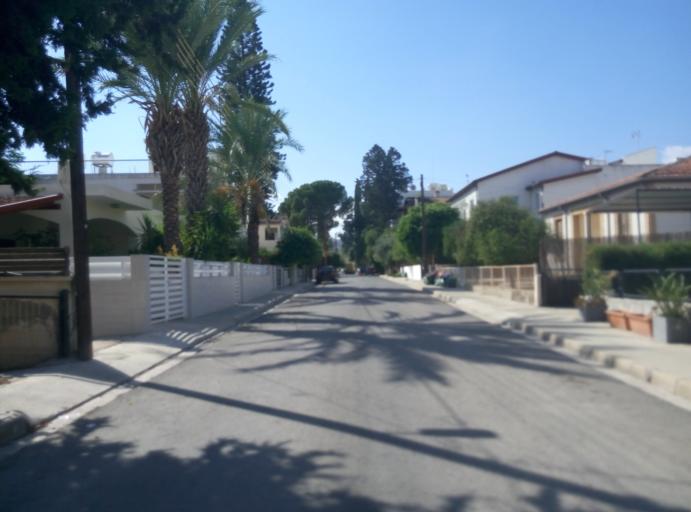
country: CY
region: Lefkosia
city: Nicosia
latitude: 35.1762
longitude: 33.3399
